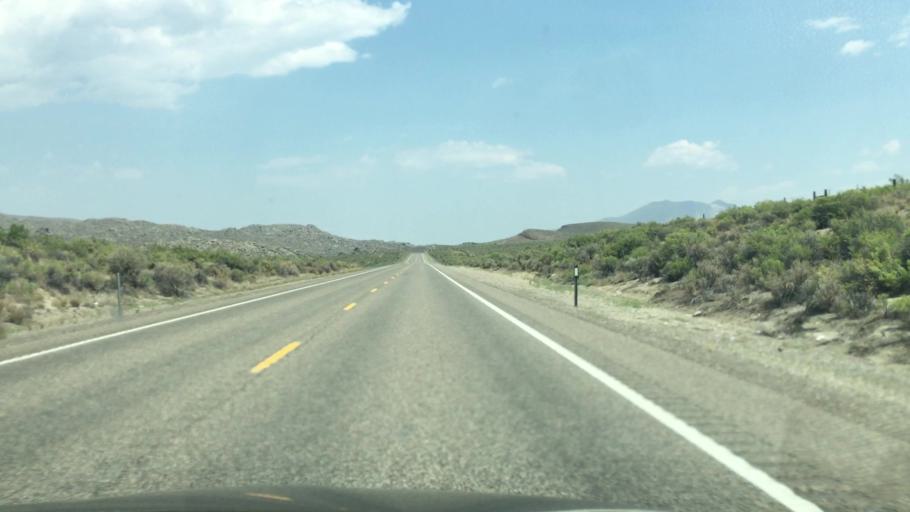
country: US
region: Nevada
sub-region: Elko County
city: Jackpot
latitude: 41.7255
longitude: -114.7978
